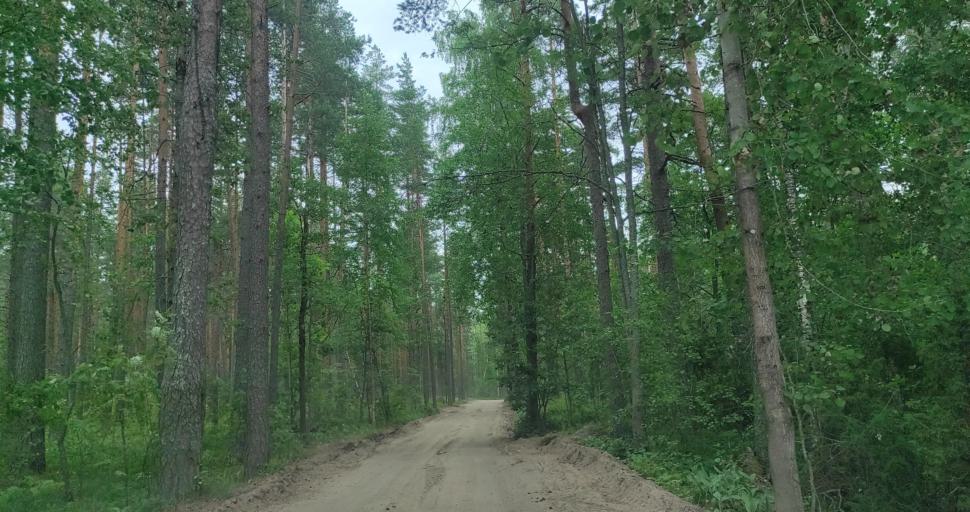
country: RU
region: Leningrad
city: Sapernoye
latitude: 60.6782
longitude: 29.9672
